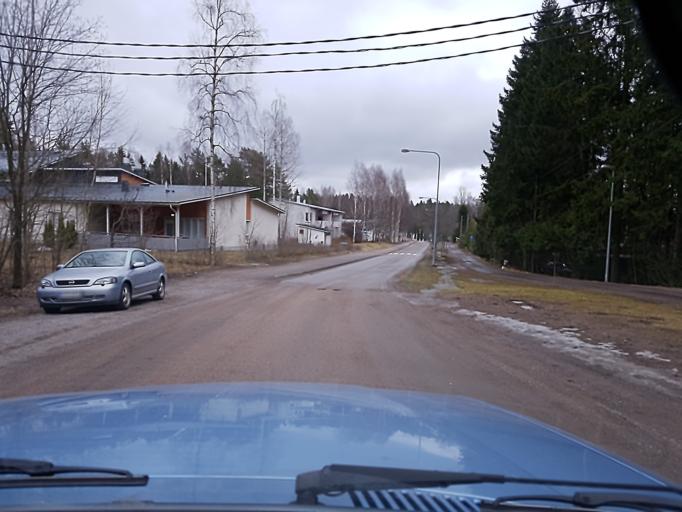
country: FI
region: Uusimaa
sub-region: Helsinki
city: Kauniainen
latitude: 60.2026
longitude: 24.7236
